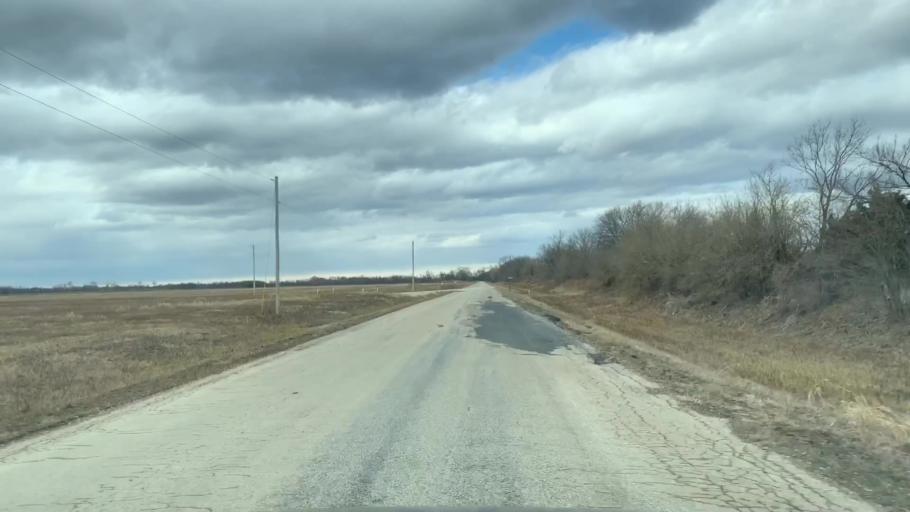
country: US
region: Kansas
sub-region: Allen County
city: Humboldt
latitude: 37.7900
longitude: -95.4706
